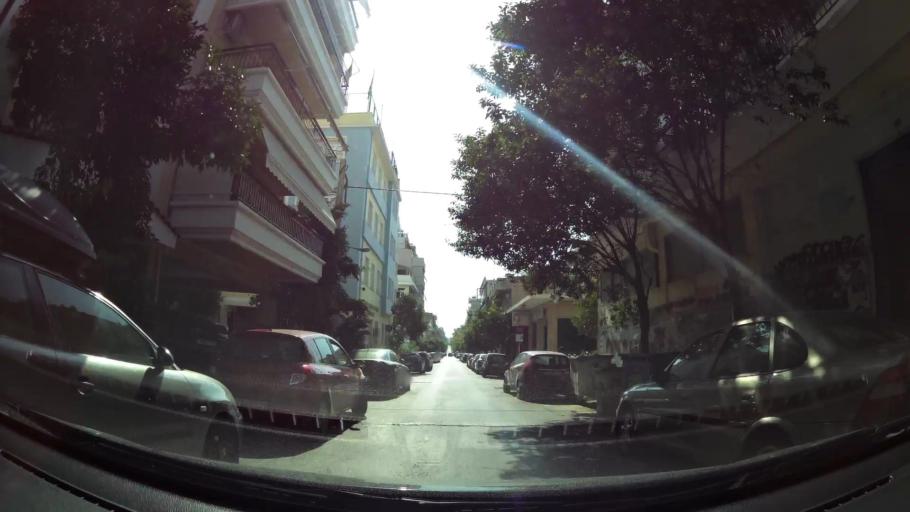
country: GR
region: Attica
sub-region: Nomos Piraios
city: Keratsini
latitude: 37.9591
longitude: 23.6311
